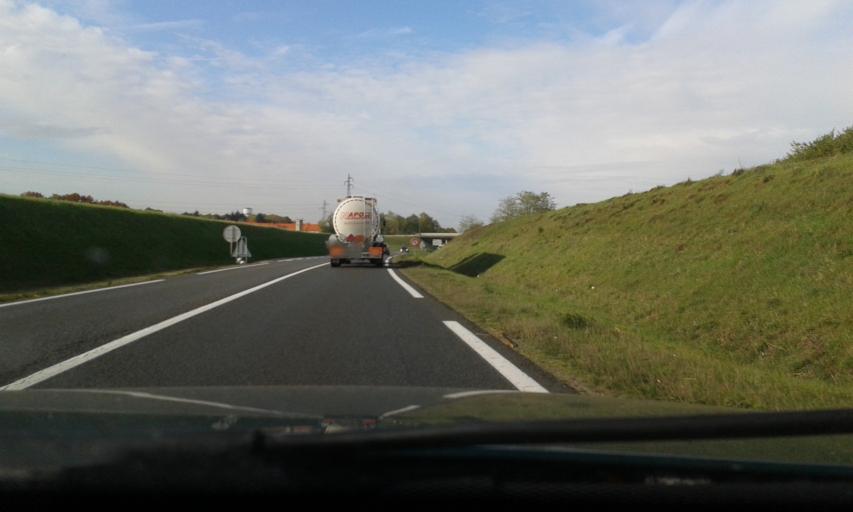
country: FR
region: Centre
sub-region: Departement du Loiret
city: Olivet
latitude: 47.8418
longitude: 1.8952
